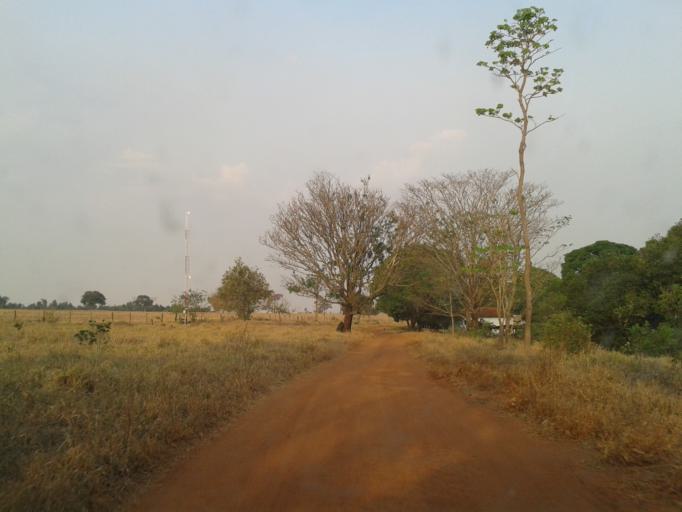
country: BR
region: Minas Gerais
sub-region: Capinopolis
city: Capinopolis
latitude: -18.8080
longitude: -49.7324
